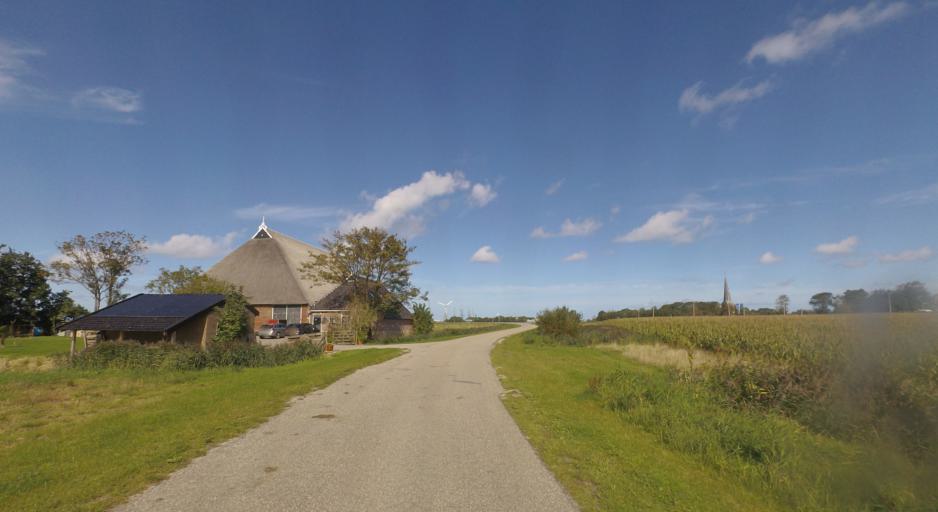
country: NL
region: Friesland
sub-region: Gemeente Dongeradeel
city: Holwerd
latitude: 53.3667
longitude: 5.8940
